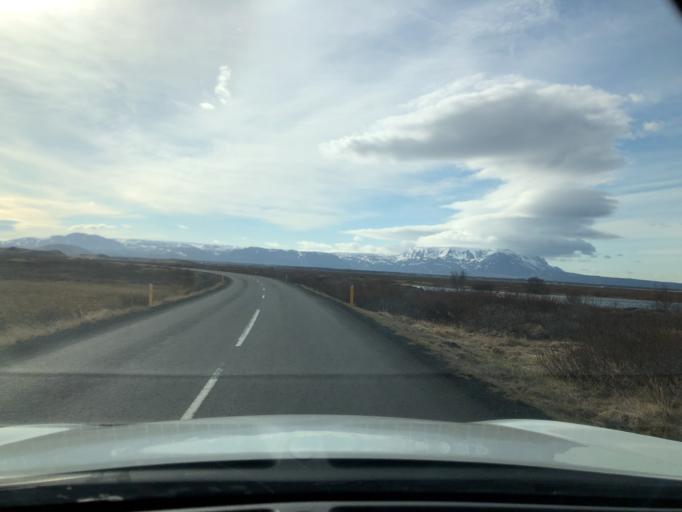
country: IS
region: Northeast
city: Laugar
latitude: 65.5650
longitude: -17.0227
